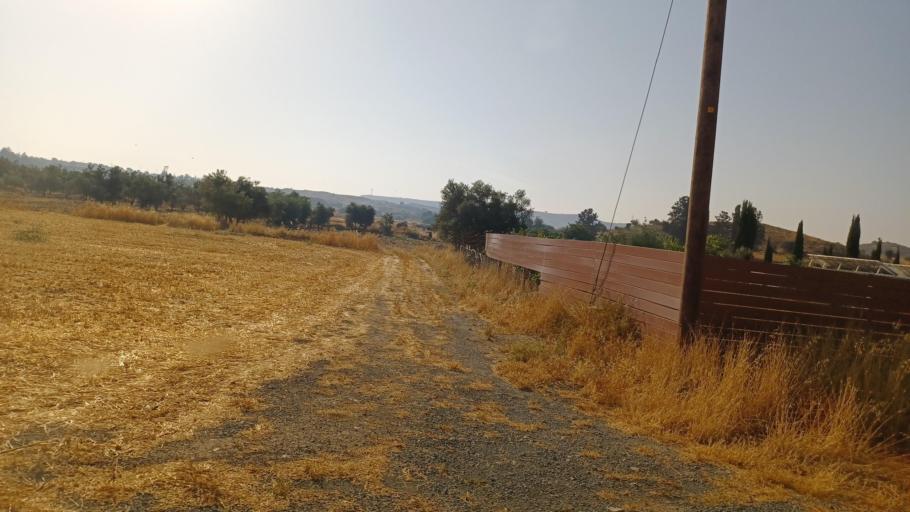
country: CY
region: Lefkosia
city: Lympia
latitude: 34.9922
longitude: 33.4376
